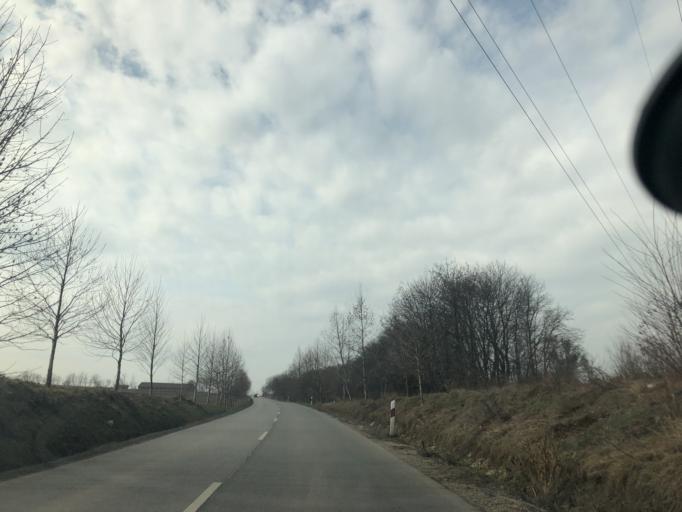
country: HU
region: Pest
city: Biatorbagy
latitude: 47.4580
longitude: 18.7908
